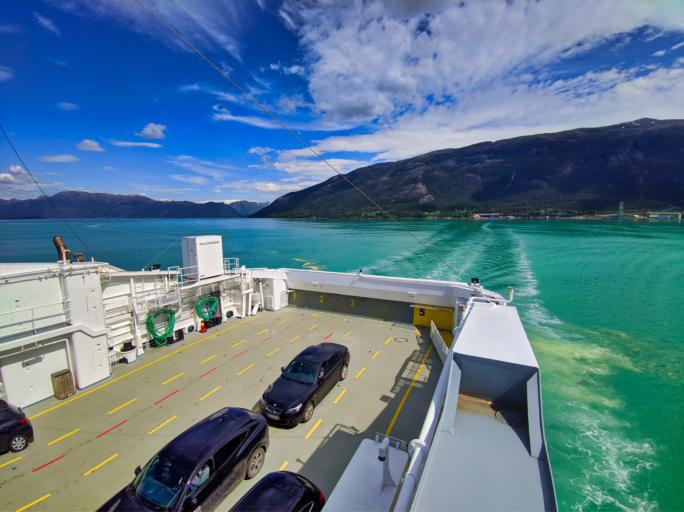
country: NO
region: Hordaland
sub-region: Kvinnherad
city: Rosendal
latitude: 60.0589
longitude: 5.9993
